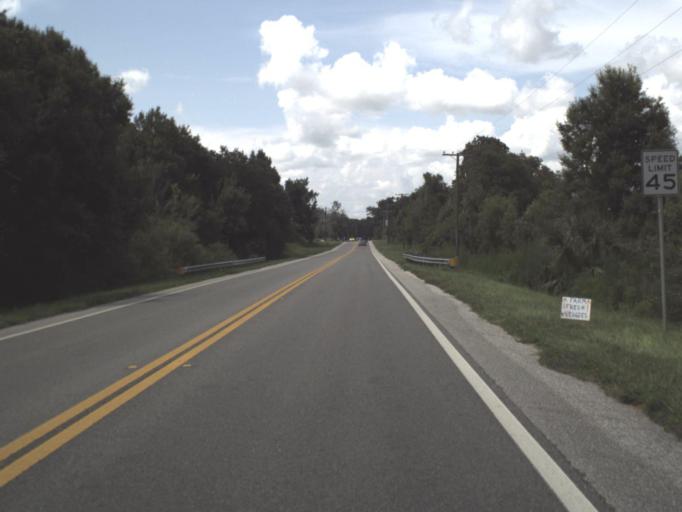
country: US
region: Florida
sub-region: Hernando County
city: Brooksville
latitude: 28.5759
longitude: -82.3752
